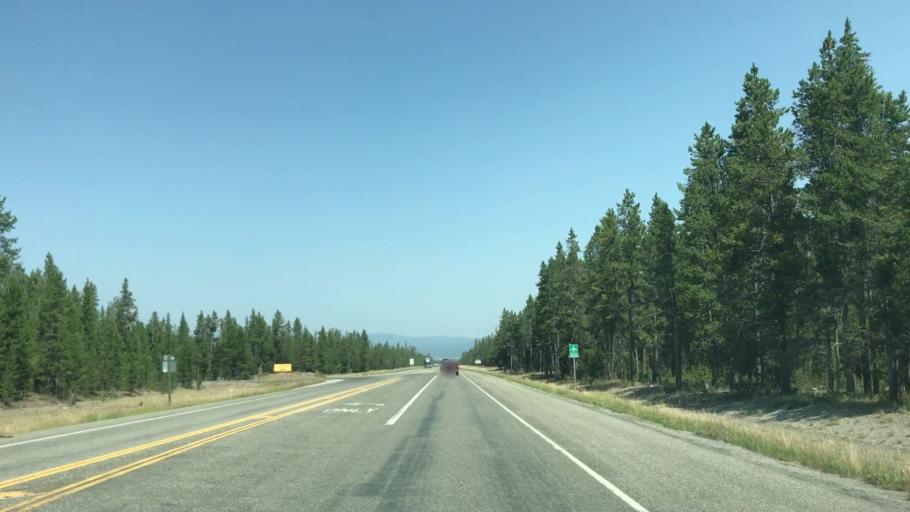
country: US
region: Montana
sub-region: Gallatin County
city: West Yellowstone
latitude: 44.6860
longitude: -111.1011
